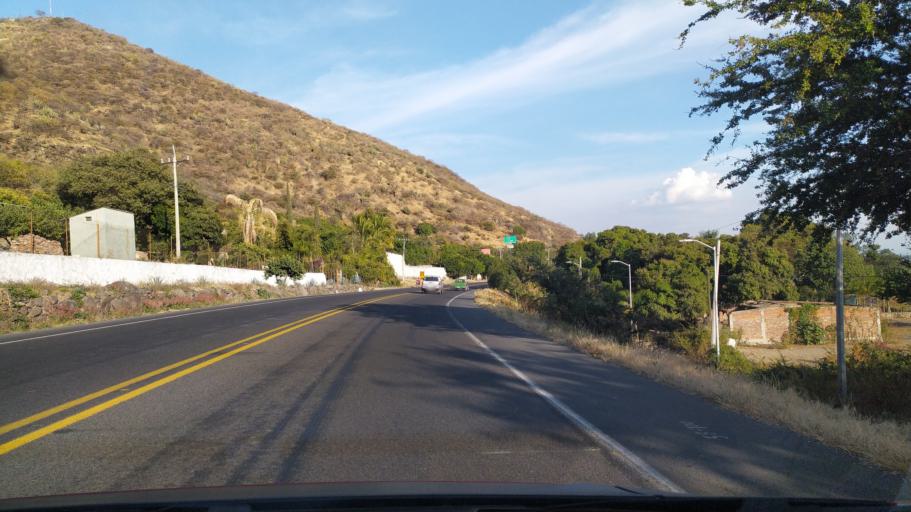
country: MX
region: Jalisco
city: Jamay
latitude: 20.2943
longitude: -102.7373
